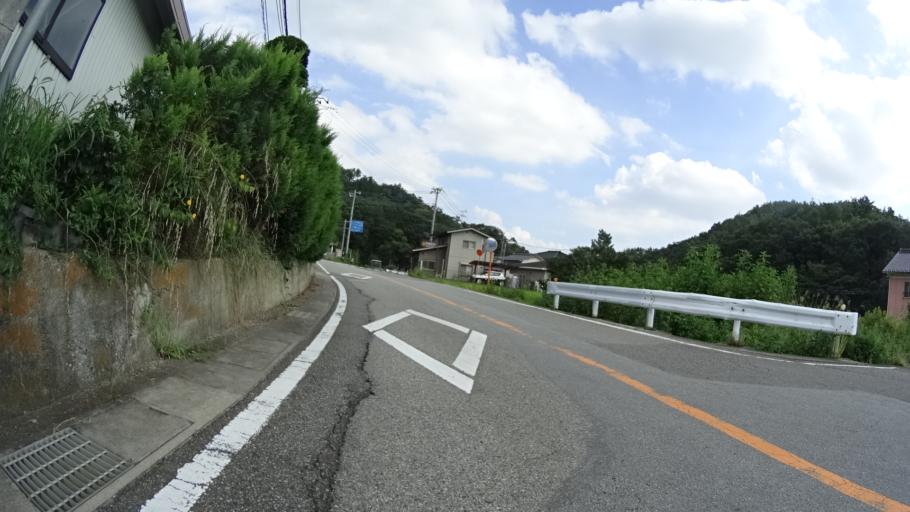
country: JP
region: Yamanashi
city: Kofu-shi
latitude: 35.7034
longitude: 138.5581
